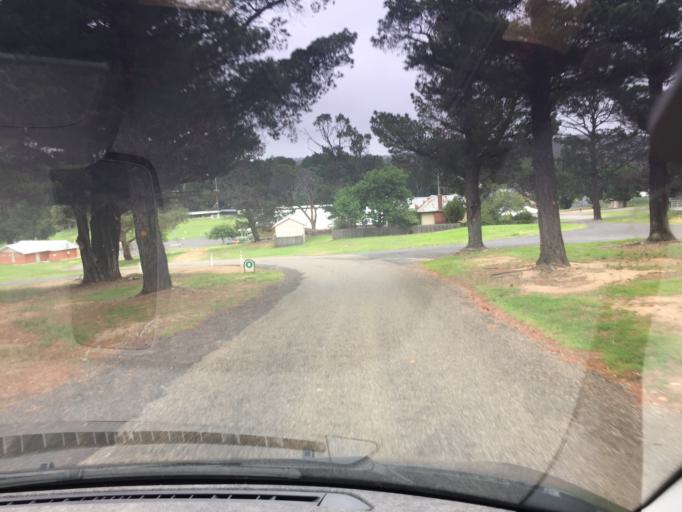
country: AU
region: New South Wales
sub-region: Cooma-Monaro
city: Cooma
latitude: -36.2399
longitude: 149.1237
